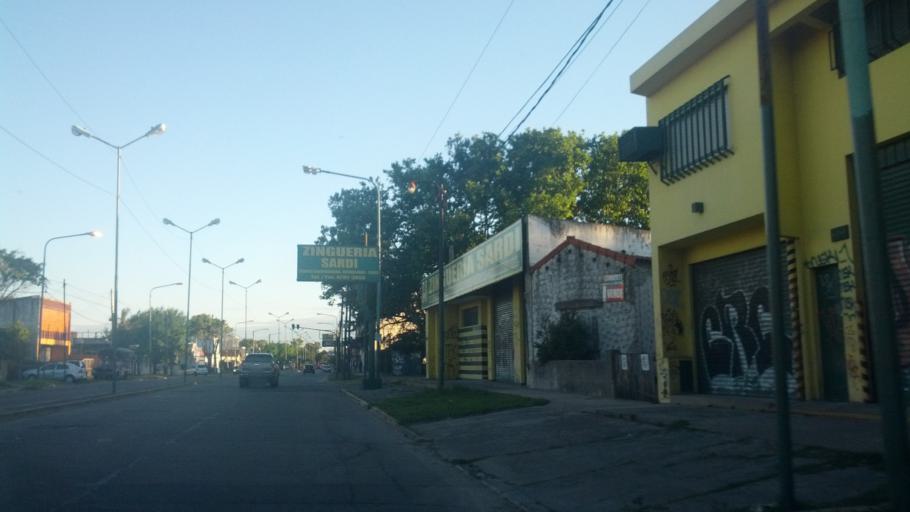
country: AR
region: Buenos Aires
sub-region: Partido de Almirante Brown
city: Adrogue
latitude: -34.7835
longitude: -58.3895
